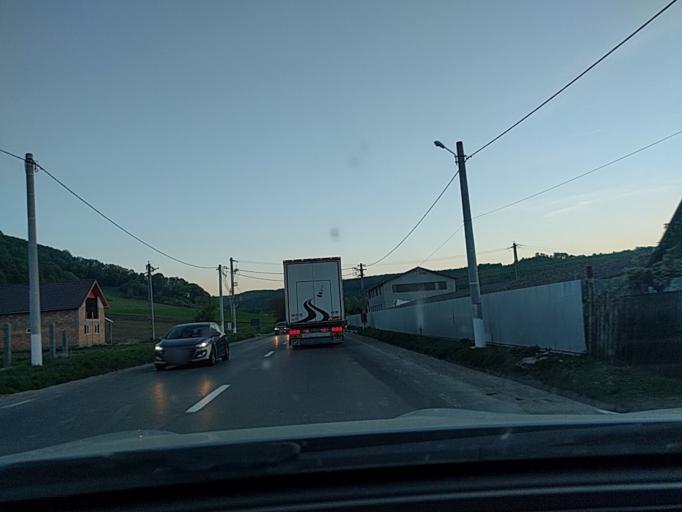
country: RO
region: Mures
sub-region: Comuna Nades
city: Nades
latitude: 46.3446
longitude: 24.7149
